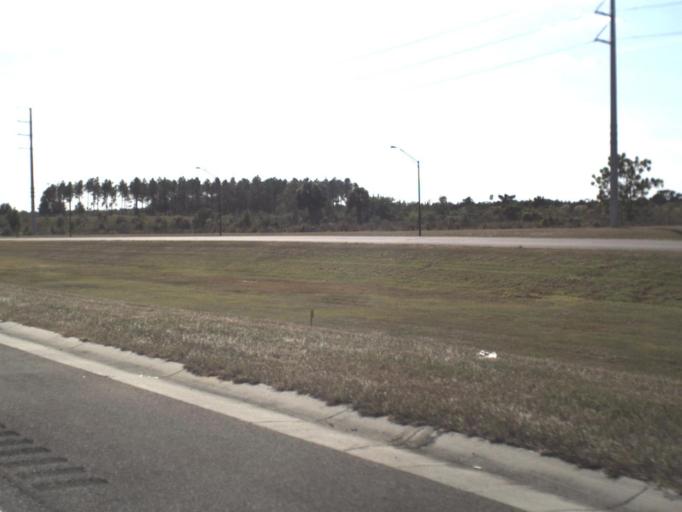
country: US
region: Florida
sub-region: Polk County
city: Citrus Ridge
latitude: 28.4165
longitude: -81.6309
